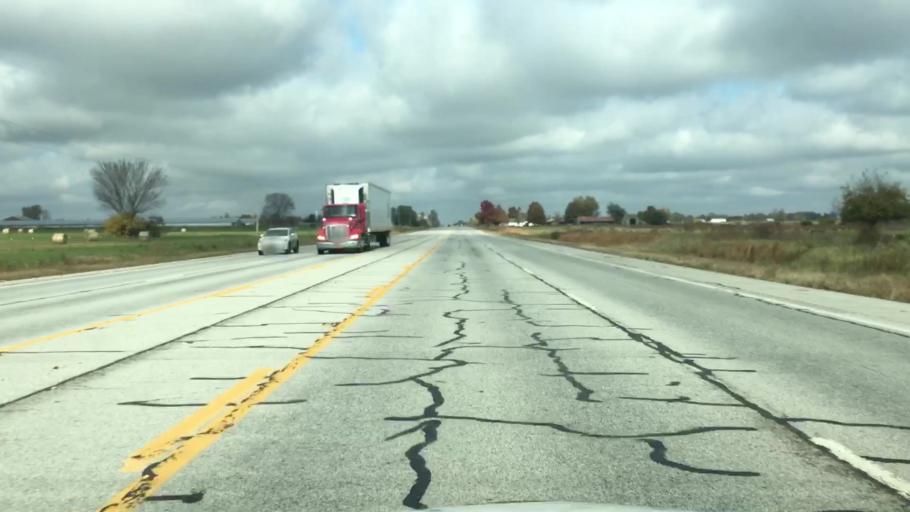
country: US
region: Arkansas
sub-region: Benton County
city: Siloam Springs
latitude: 36.2135
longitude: -94.4955
